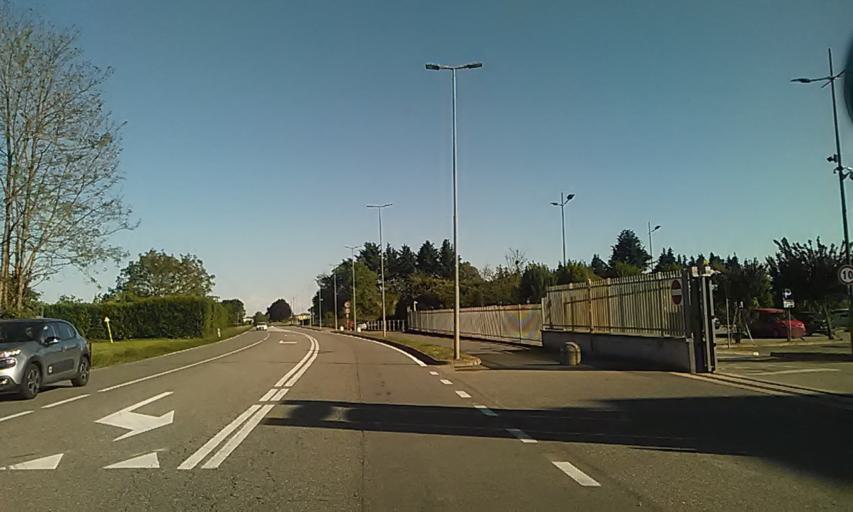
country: IT
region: Piedmont
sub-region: Provincia di Novara
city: Momo
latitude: 45.5871
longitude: 8.5455
